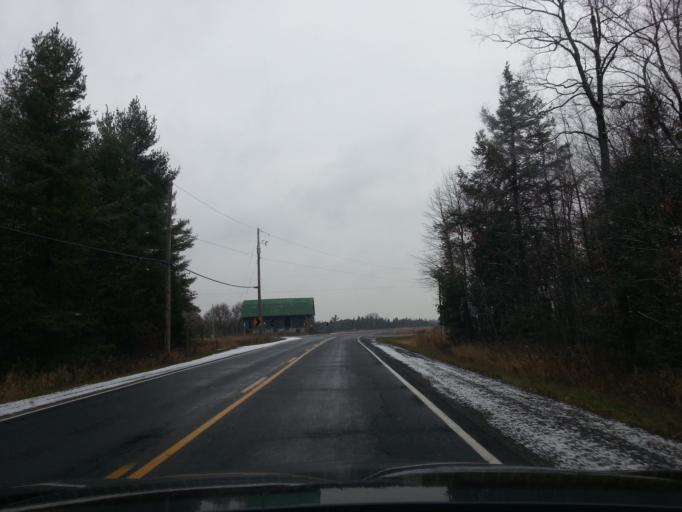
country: CA
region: Ontario
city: Carleton Place
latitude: 45.1002
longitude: -76.0315
